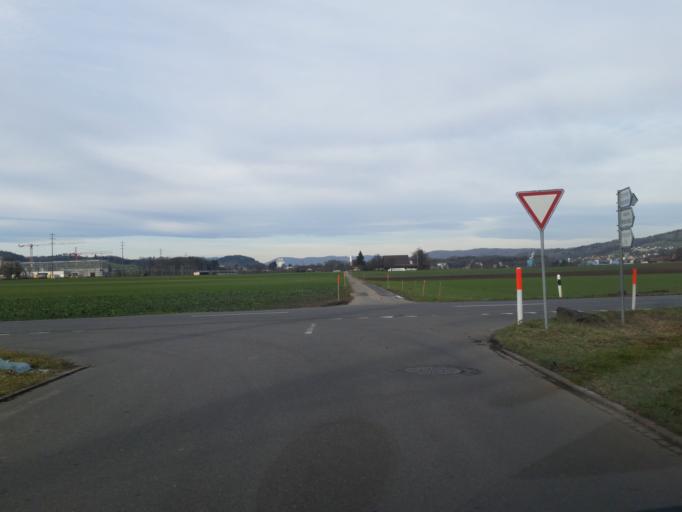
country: CH
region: Aargau
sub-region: Bezirk Bremgarten
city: Villmergen
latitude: 47.3571
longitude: 8.2609
